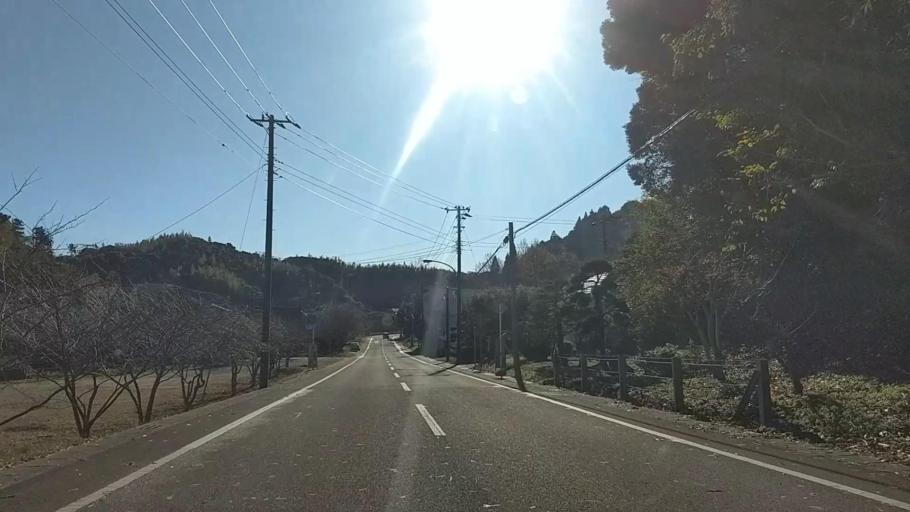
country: JP
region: Chiba
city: Futtsu
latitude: 35.2425
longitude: 139.8730
